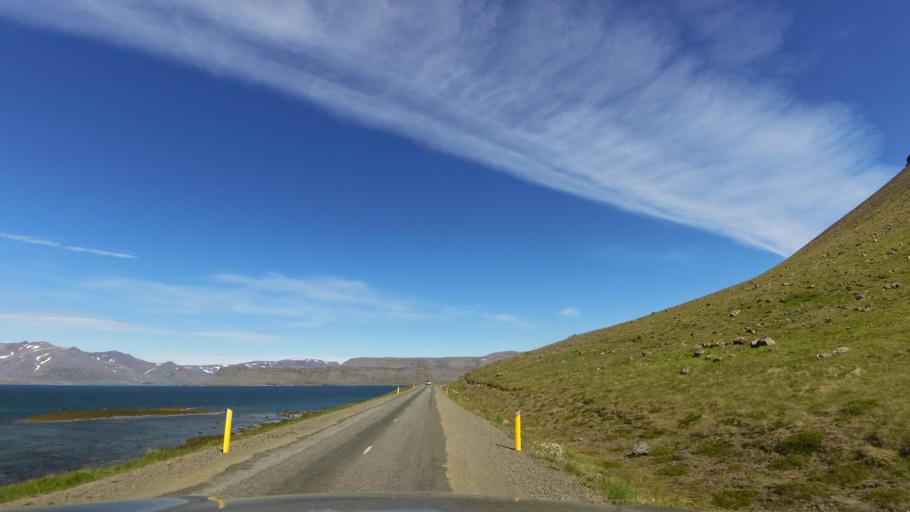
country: IS
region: Westfjords
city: Isafjoerdur
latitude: 65.6802
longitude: -23.5859
